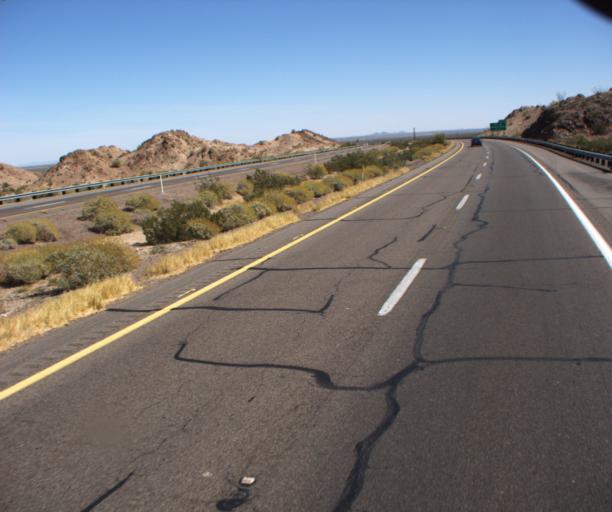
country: US
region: Arizona
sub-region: Yuma County
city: Wellton
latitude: 32.7257
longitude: -113.7460
